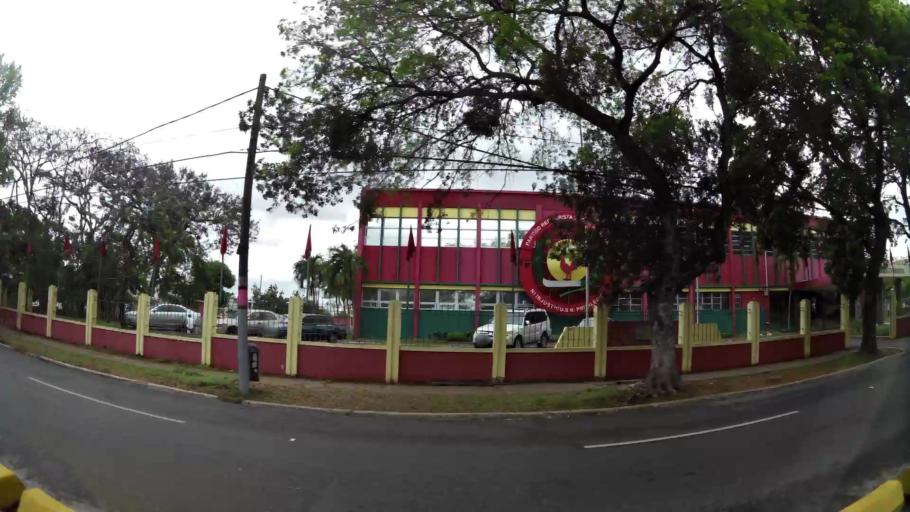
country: DO
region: Nacional
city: La Agustina
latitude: 18.4886
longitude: -69.9296
